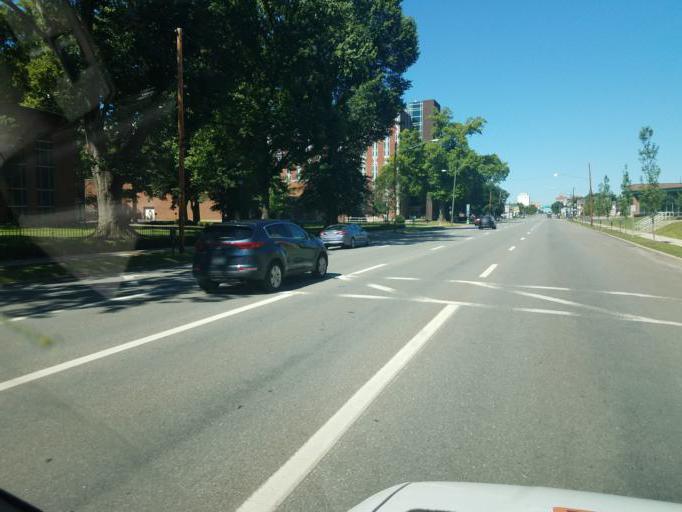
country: US
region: West Virginia
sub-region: Cabell County
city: Huntington
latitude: 38.4245
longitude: -82.4295
